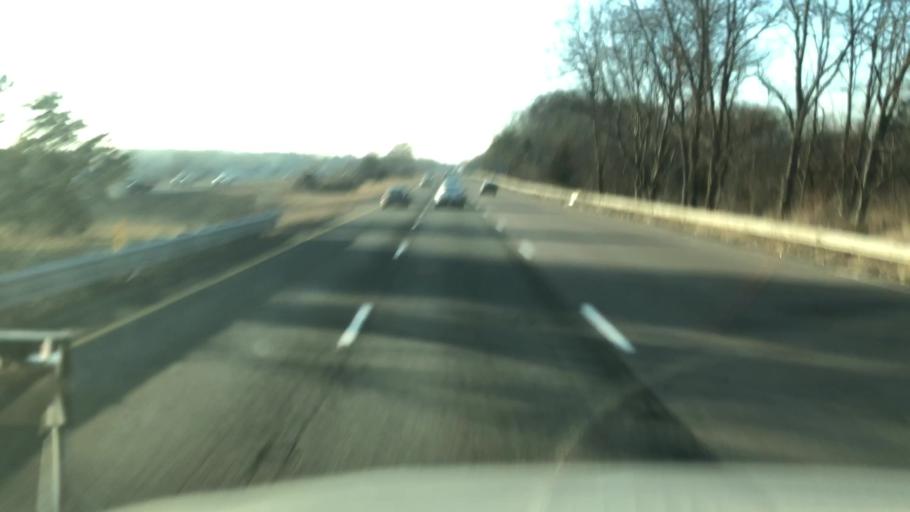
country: US
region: Massachusetts
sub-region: Bristol County
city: Seekonk
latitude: 41.8023
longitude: -71.3304
